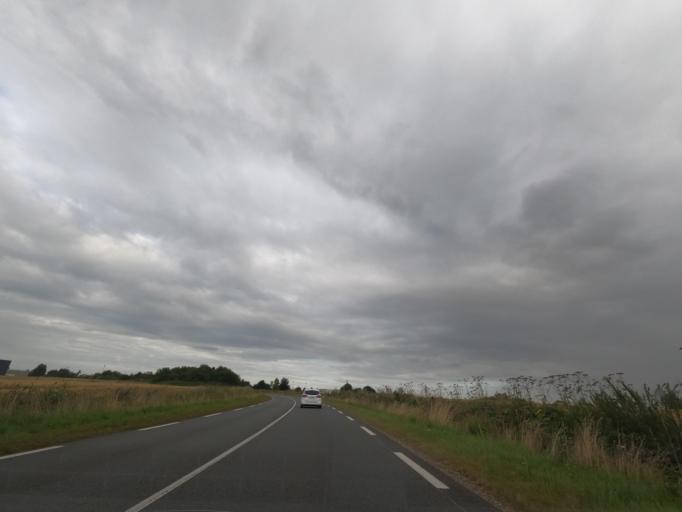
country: FR
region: Haute-Normandie
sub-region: Departement de l'Eure
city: Bourgtheroulde-Infreville
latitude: 49.2918
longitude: 0.8710
